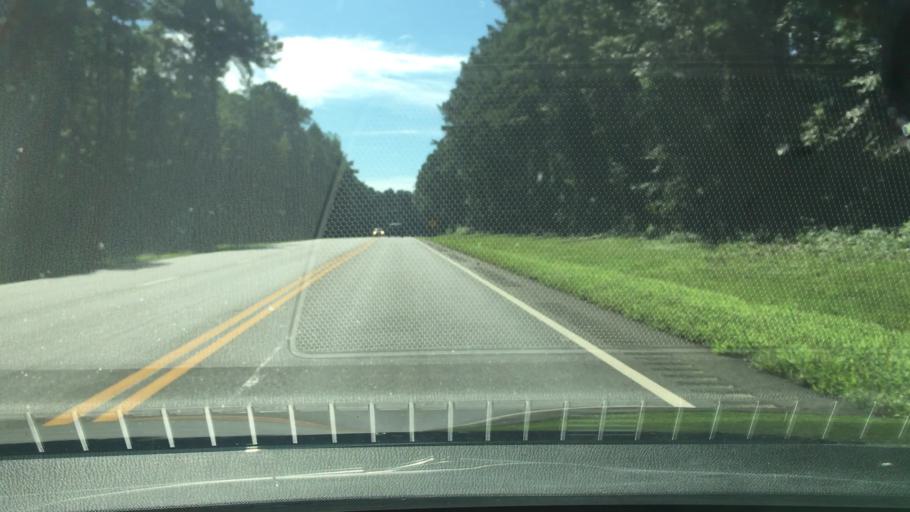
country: US
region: Georgia
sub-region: Putnam County
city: Jefferson
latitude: 33.4366
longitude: -83.3826
